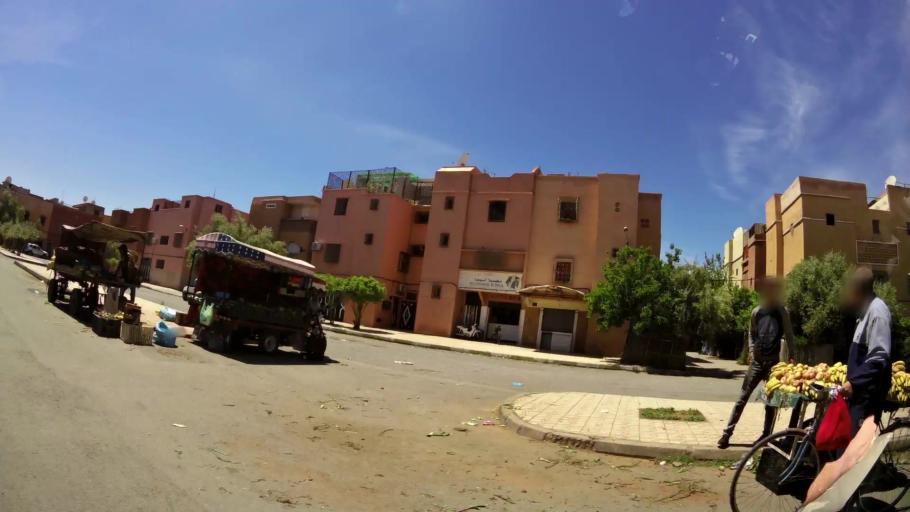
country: MA
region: Marrakech-Tensift-Al Haouz
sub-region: Marrakech
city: Marrakesh
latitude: 31.6324
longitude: -8.0472
